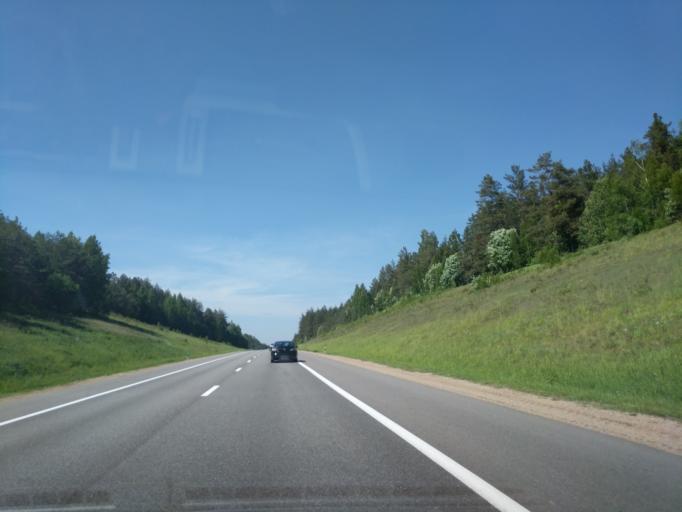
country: BY
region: Grodnenskaya
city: Kreva
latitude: 54.2555
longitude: 26.3173
